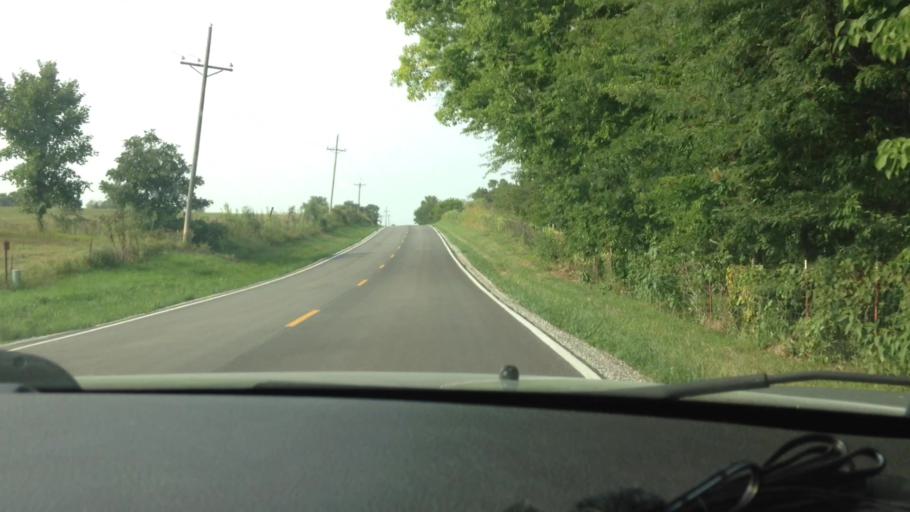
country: US
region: Missouri
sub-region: Platte County
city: Platte City
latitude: 39.4269
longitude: -94.7798
